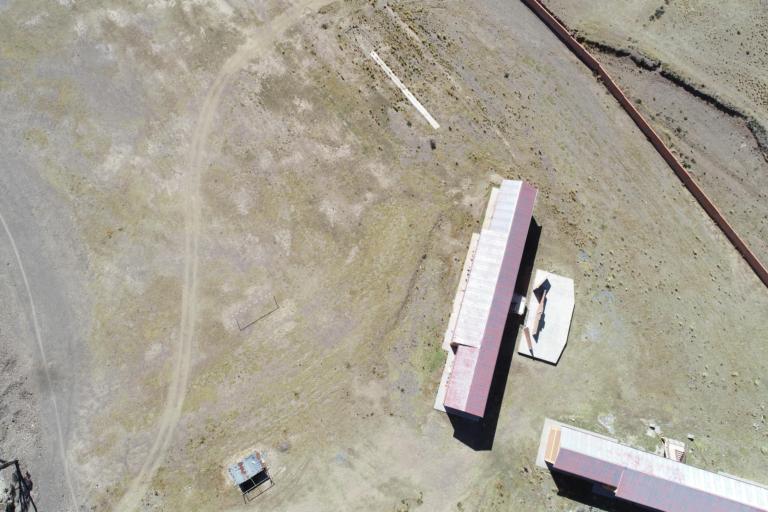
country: BO
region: La Paz
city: Achacachi
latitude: -15.8976
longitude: -68.9018
